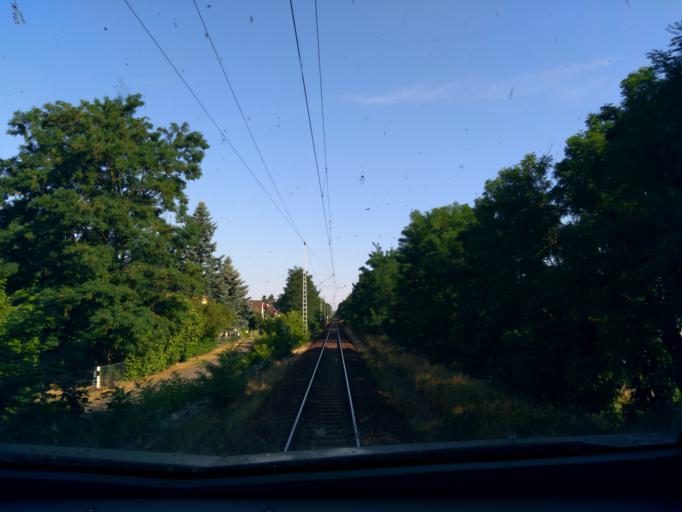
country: DE
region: Brandenburg
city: Vetschau
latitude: 51.8163
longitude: 14.0319
